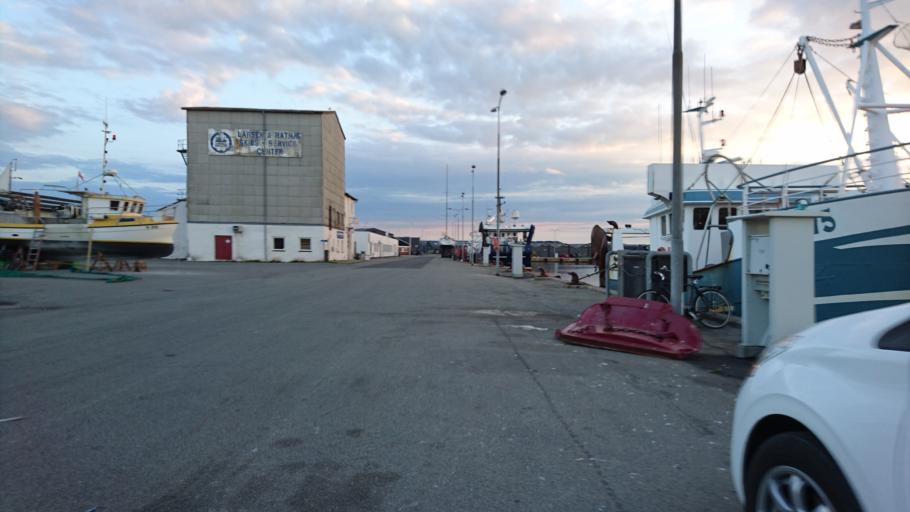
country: DK
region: North Denmark
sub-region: Frederikshavn Kommune
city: Skagen
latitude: 57.7159
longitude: 10.5861
